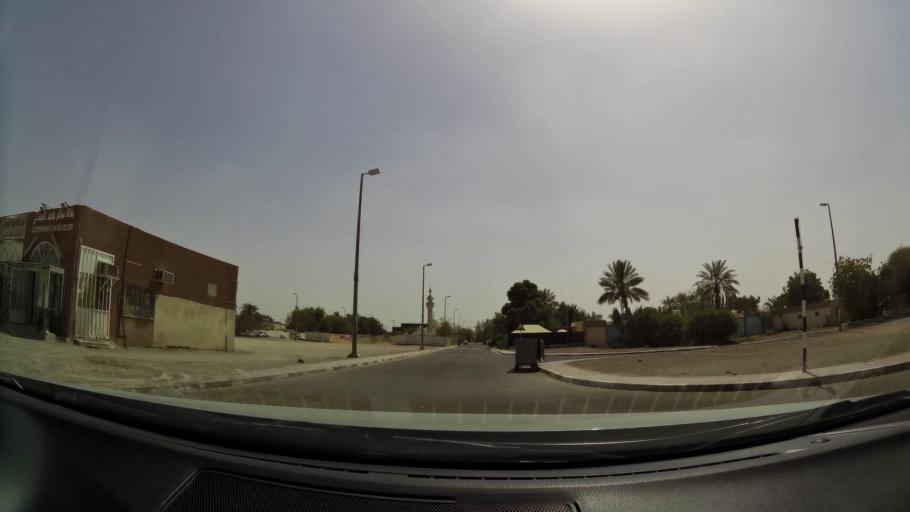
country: AE
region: Abu Dhabi
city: Al Ain
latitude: 24.2281
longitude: 55.6974
